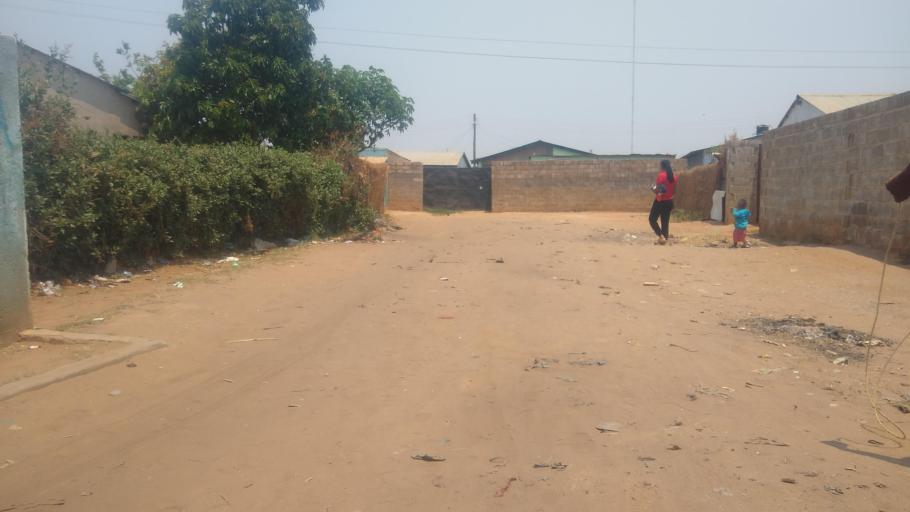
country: ZM
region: Lusaka
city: Lusaka
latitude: -15.4383
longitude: 28.3773
